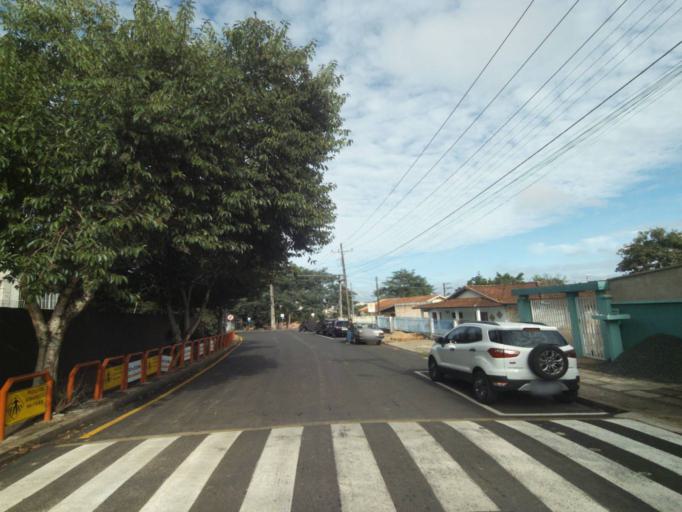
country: BR
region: Parana
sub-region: Telemaco Borba
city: Telemaco Borba
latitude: -24.3389
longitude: -50.6112
